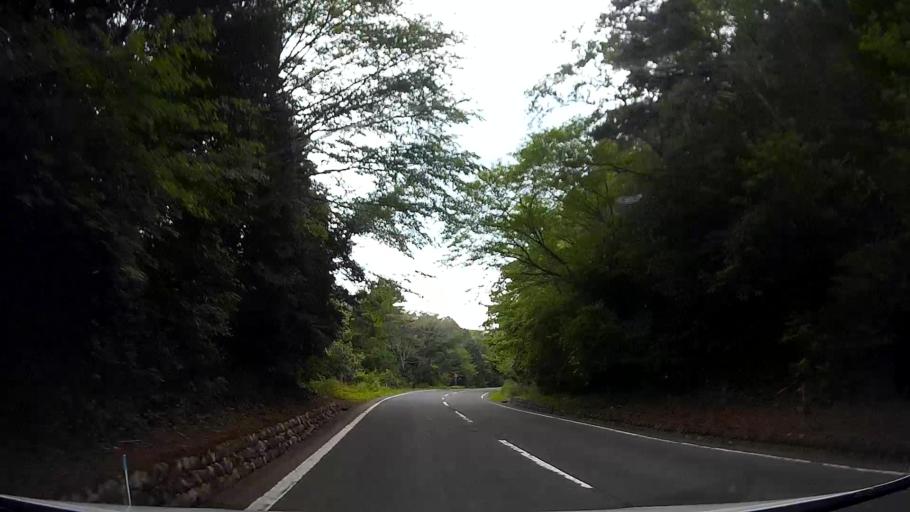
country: JP
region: Shizuoka
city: Ito
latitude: 34.9894
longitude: 139.0391
